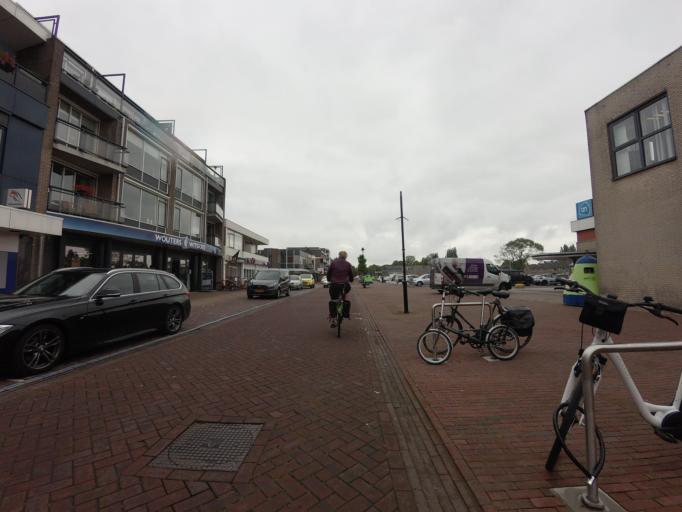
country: NL
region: North Holland
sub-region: Gemeente Schagen
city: Schagen
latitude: 52.7880
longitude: 4.7964
